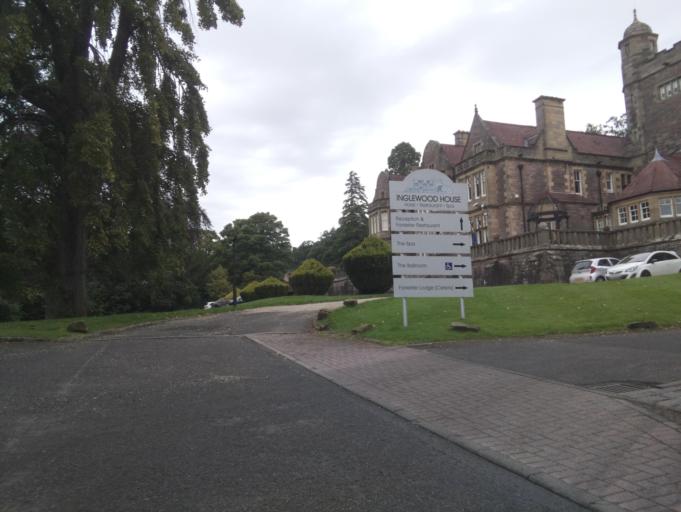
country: GB
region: Scotland
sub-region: Clackmannanshire
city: Alloa
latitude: 56.1261
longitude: -3.8036
